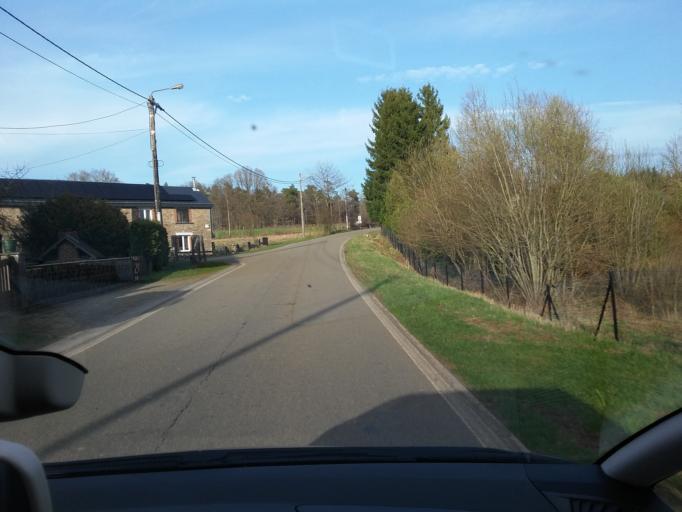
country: BE
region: Wallonia
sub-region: Province du Luxembourg
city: Daverdisse
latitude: 50.0122
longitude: 5.1718
